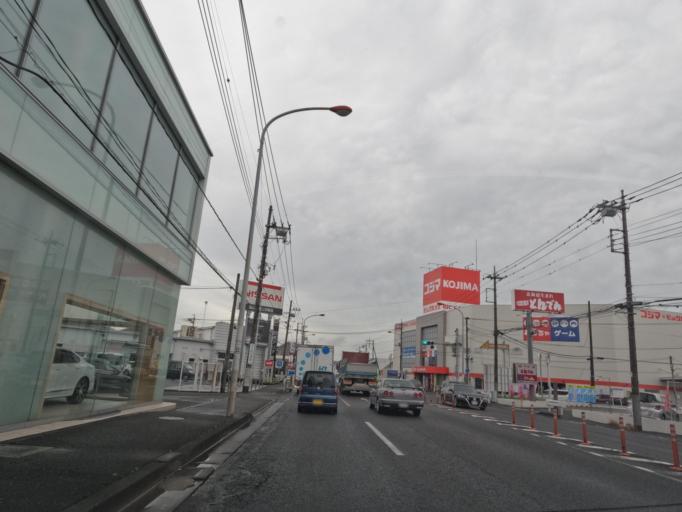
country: JP
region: Saitama
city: Koshigaya
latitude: 35.9041
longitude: 139.7672
